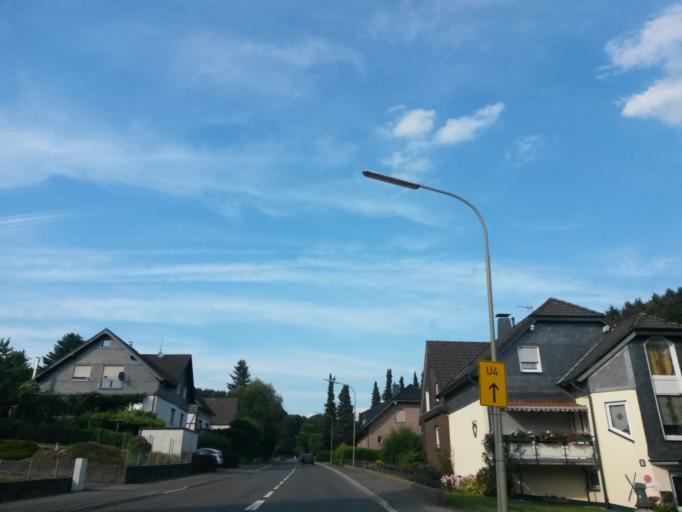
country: DE
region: North Rhine-Westphalia
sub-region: Regierungsbezirk Koln
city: Lindlar
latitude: 51.0230
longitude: 7.3903
